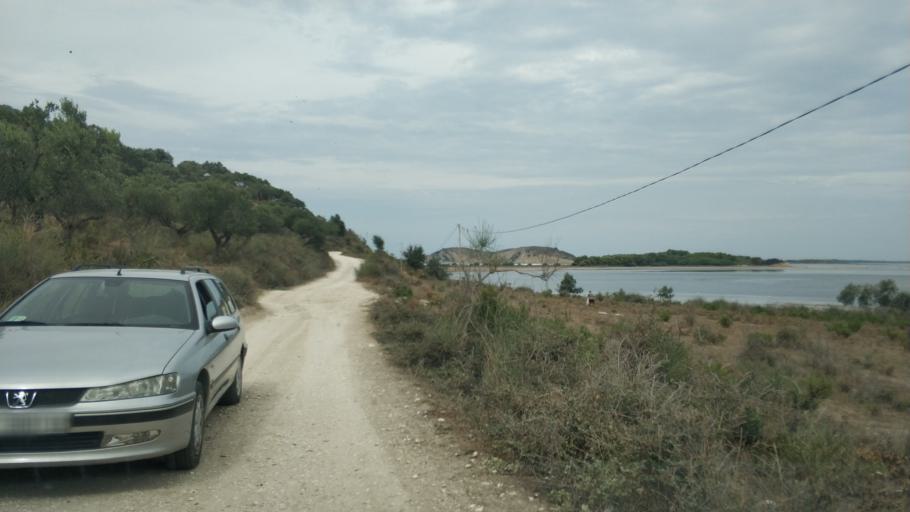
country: AL
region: Vlore
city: Vlore
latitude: 40.5169
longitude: 19.3938
